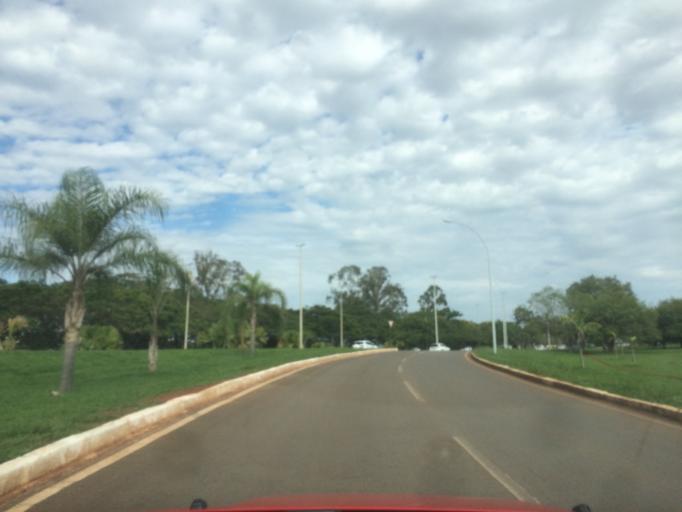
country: BR
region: Federal District
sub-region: Brasilia
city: Brasilia
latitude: -15.8015
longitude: -47.8501
